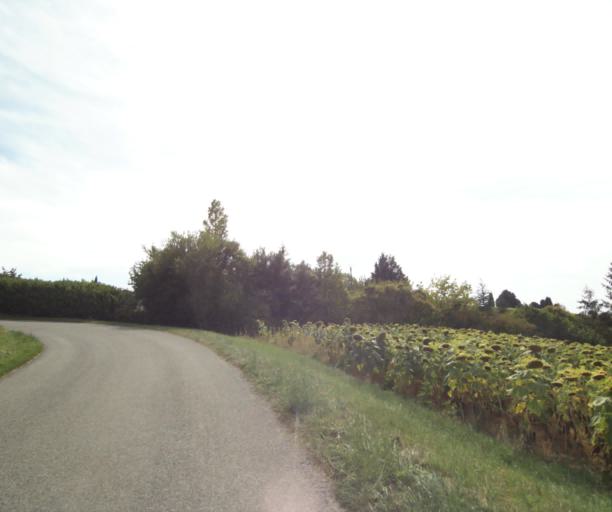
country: FR
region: Midi-Pyrenees
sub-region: Departement de l'Ariege
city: Lezat-sur-Leze
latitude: 43.2410
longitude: 1.3932
